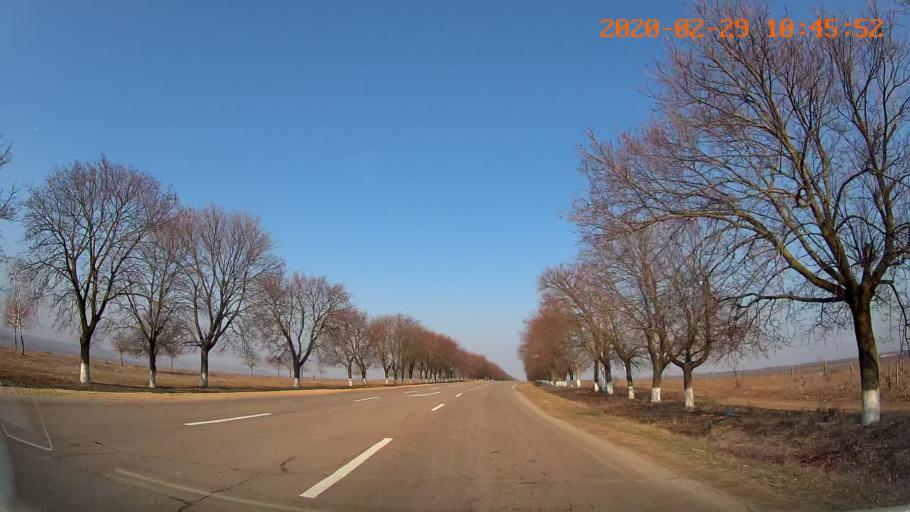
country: MD
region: Telenesti
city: Grigoriopol
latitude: 47.0794
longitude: 29.3785
